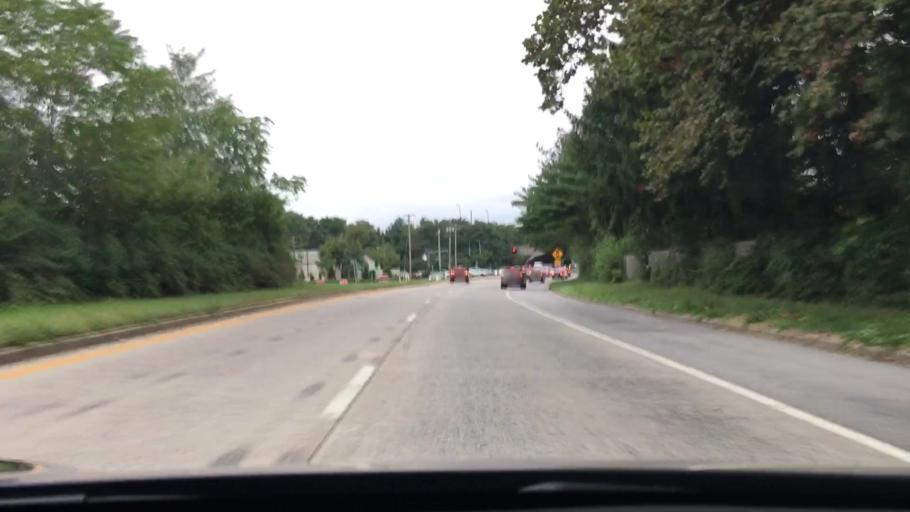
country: US
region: New York
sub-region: Nassau County
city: Carle Place
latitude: 40.7584
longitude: -73.6180
